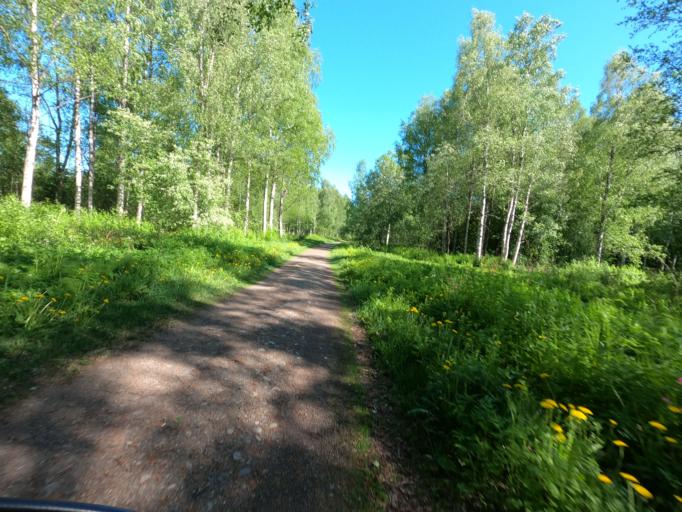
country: FI
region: North Karelia
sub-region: Joensuu
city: Joensuu
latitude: 62.6058
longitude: 29.8098
